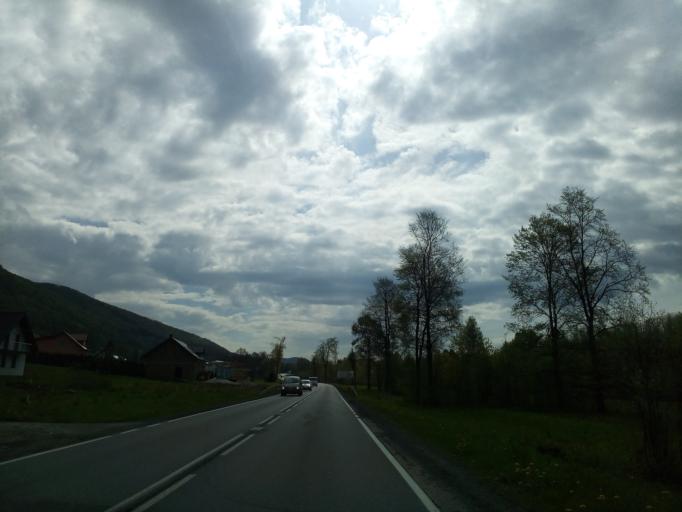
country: PL
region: Lesser Poland Voivodeship
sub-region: Powiat nowosadecki
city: Kamionka Wielka
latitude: 49.5393
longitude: 20.8028
